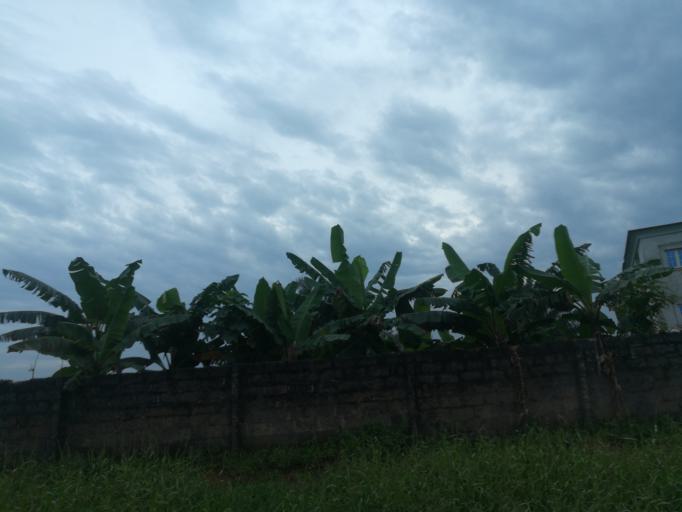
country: NG
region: Rivers
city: Port Harcourt
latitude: 4.7955
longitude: 6.9552
